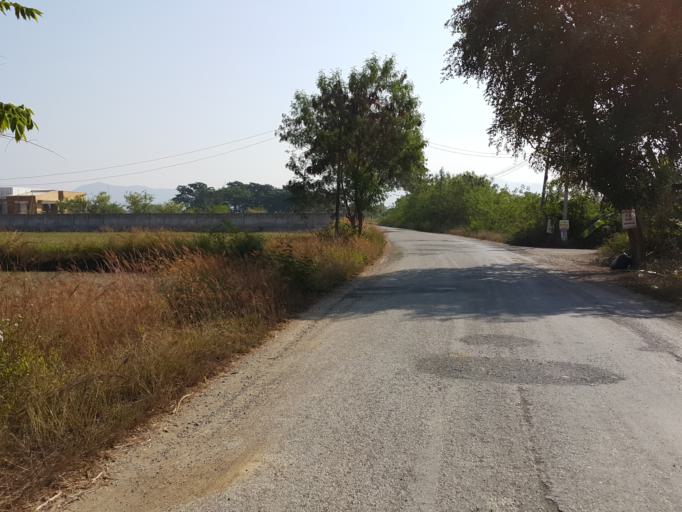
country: TH
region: Chiang Mai
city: San Kamphaeng
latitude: 18.6909
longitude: 99.1222
